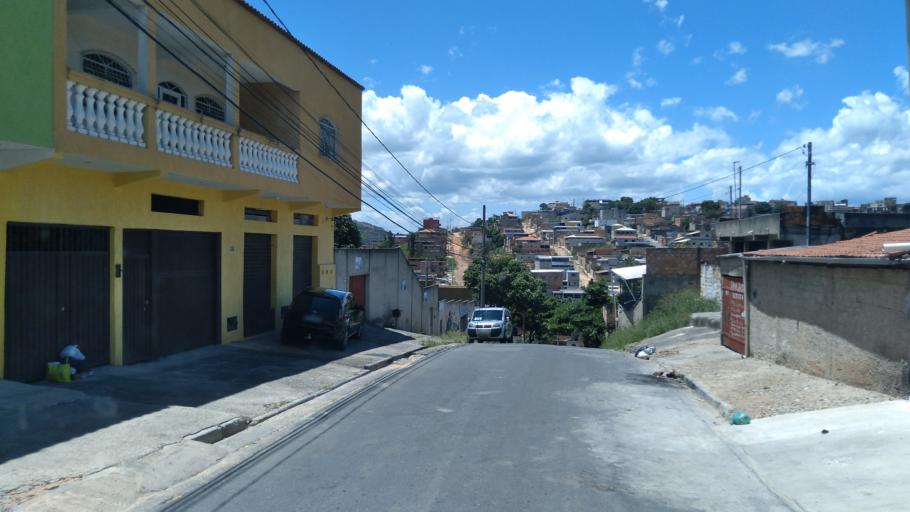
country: BR
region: Minas Gerais
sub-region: Santa Luzia
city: Santa Luzia
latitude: -19.8341
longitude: -43.8904
